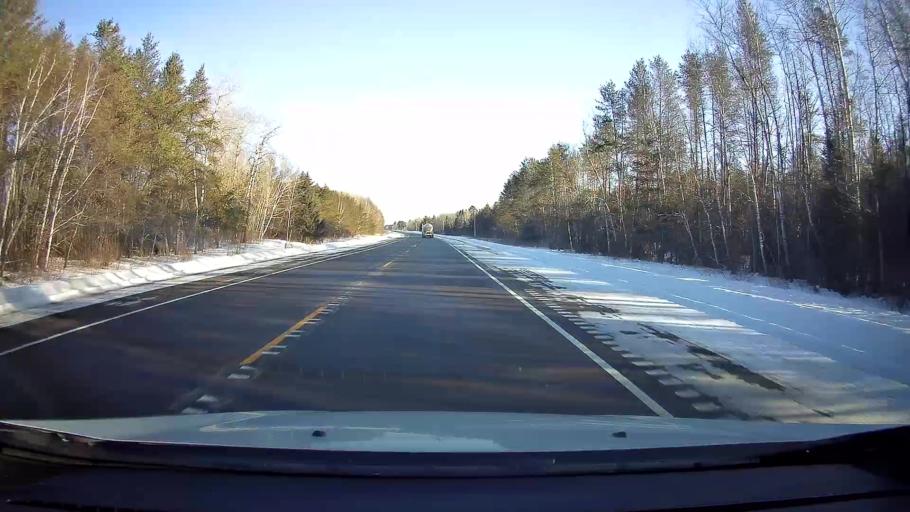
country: US
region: Wisconsin
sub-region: Sawyer County
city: Hayward
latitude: 46.0914
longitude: -91.3893
